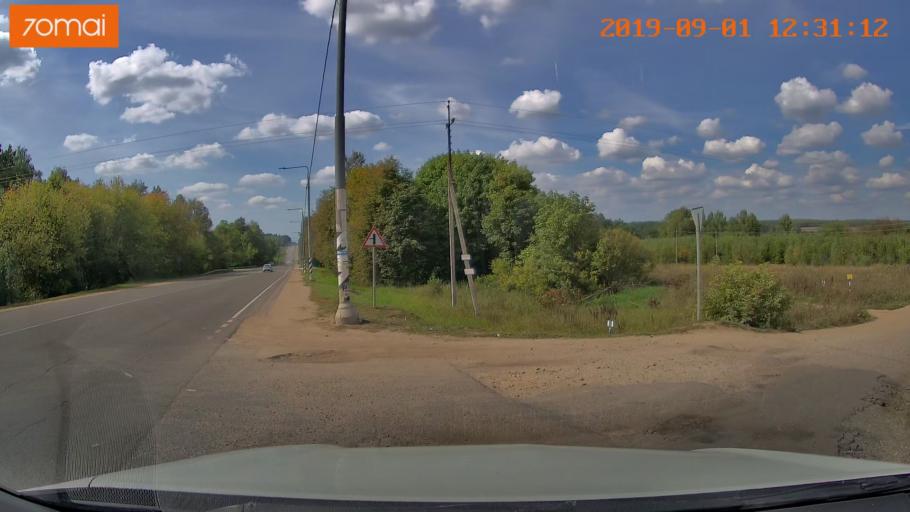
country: RU
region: Kaluga
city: Maloyaroslavets
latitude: 55.0033
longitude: 36.4200
